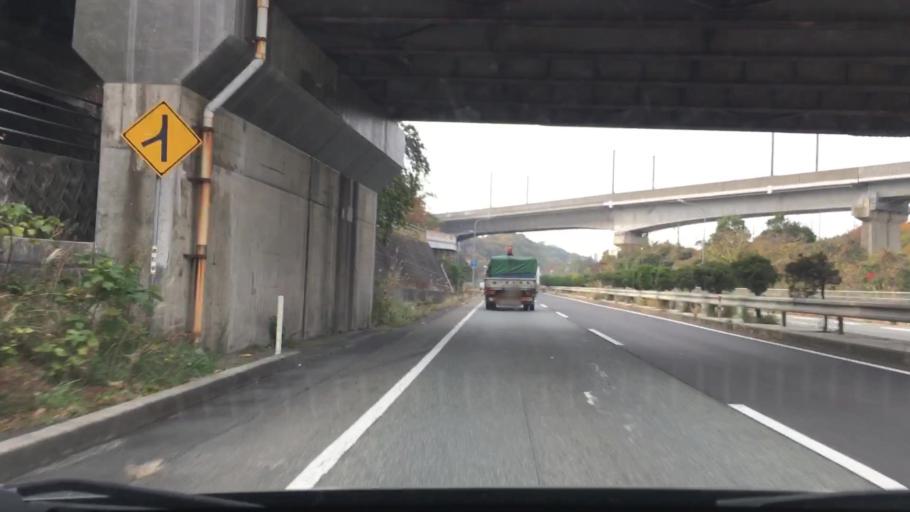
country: JP
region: Yamaguchi
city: Ogori-shimogo
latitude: 34.0550
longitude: 131.3499
